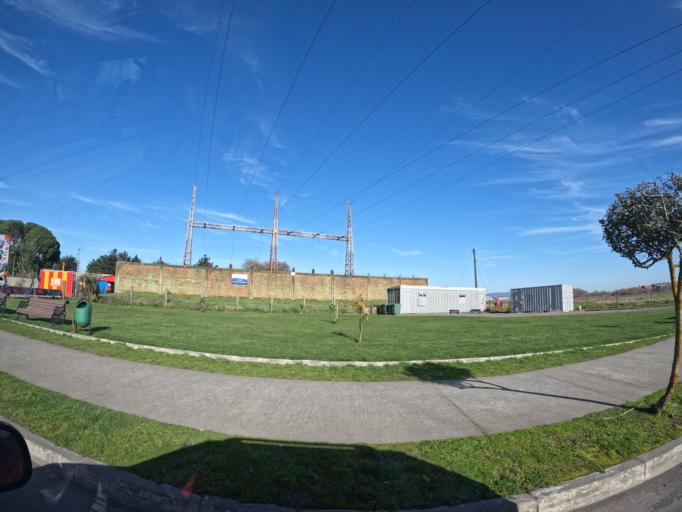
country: CL
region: Biobio
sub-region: Provincia de Concepcion
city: Concepcion
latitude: -36.7767
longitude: -73.0706
